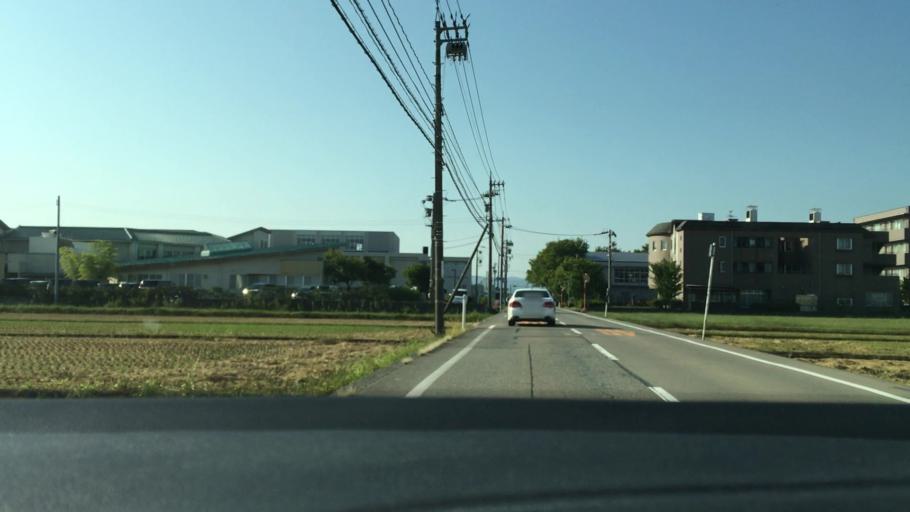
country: JP
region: Ishikawa
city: Nonoichi
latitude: 36.5171
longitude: 136.5997
